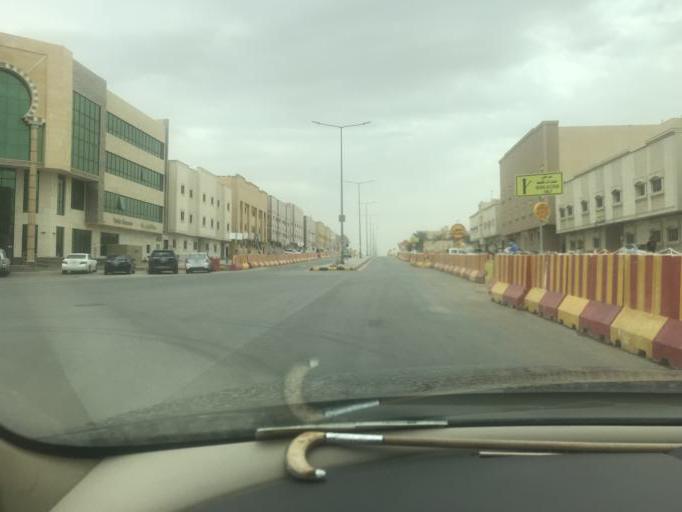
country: SA
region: Ar Riyad
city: Riyadh
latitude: 24.7955
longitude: 46.7086
